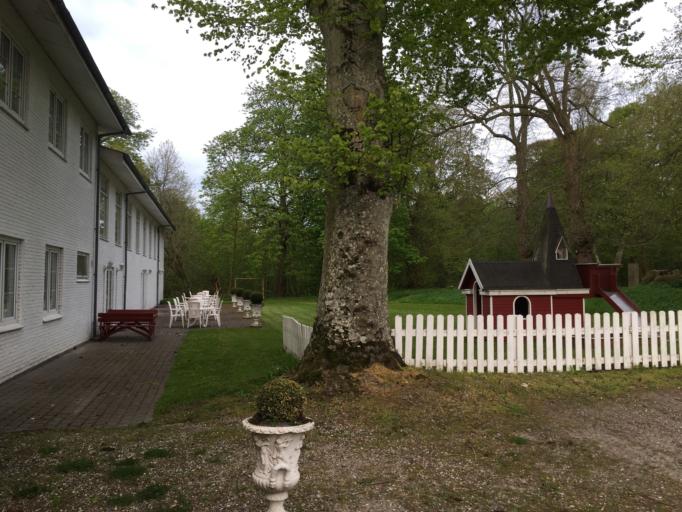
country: DK
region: North Denmark
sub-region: Alborg Kommune
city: Frejlev
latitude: 57.0053
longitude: 9.7755
